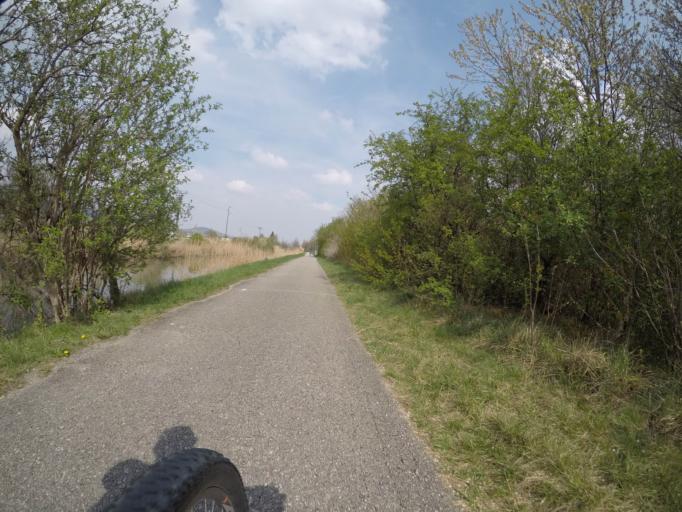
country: AT
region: Lower Austria
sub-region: Politischer Bezirk Baden
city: Traiskirchen
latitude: 48.0249
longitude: 16.2807
